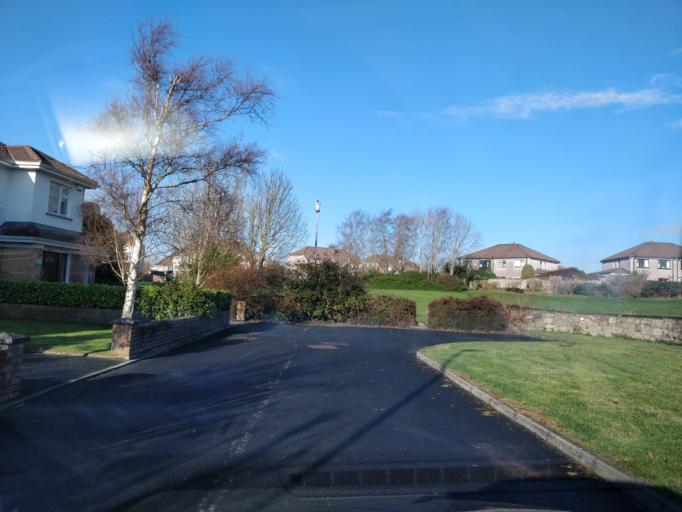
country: IE
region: Connaught
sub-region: County Galway
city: Bearna
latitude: 53.2623
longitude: -9.1196
